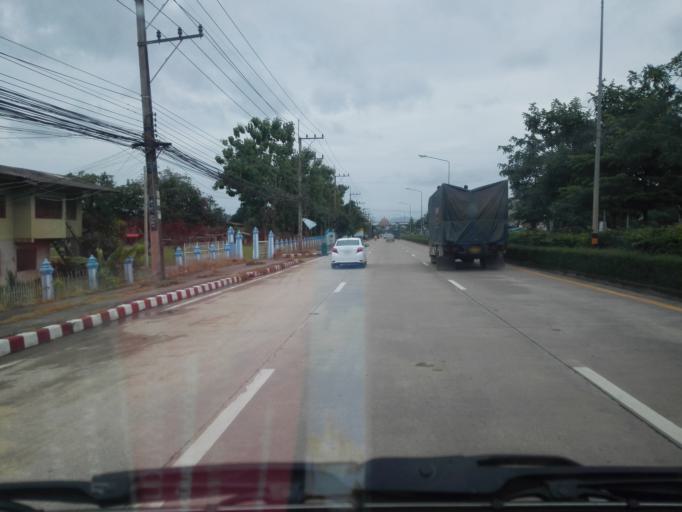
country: TH
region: Tak
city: Mae Sot
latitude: 16.7003
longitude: 98.5359
